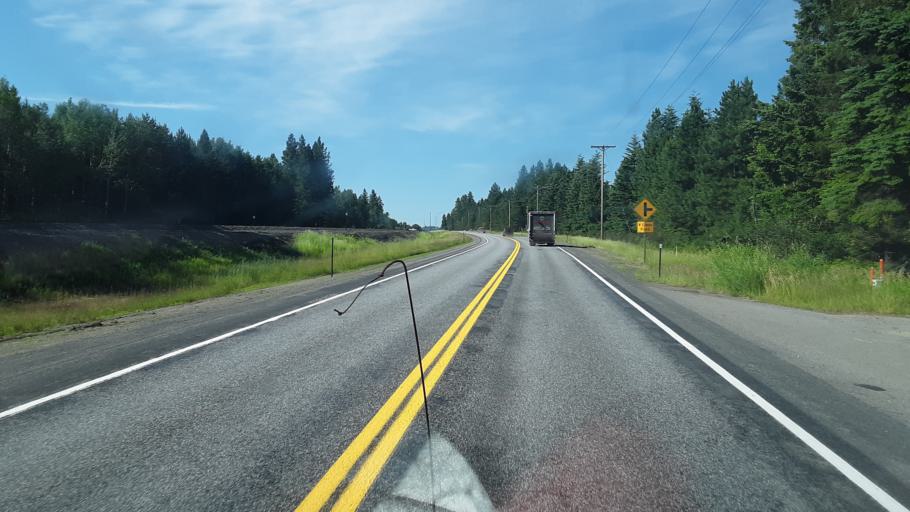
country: US
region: Idaho
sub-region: Bonner County
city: Ponderay
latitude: 48.4895
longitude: -116.4578
